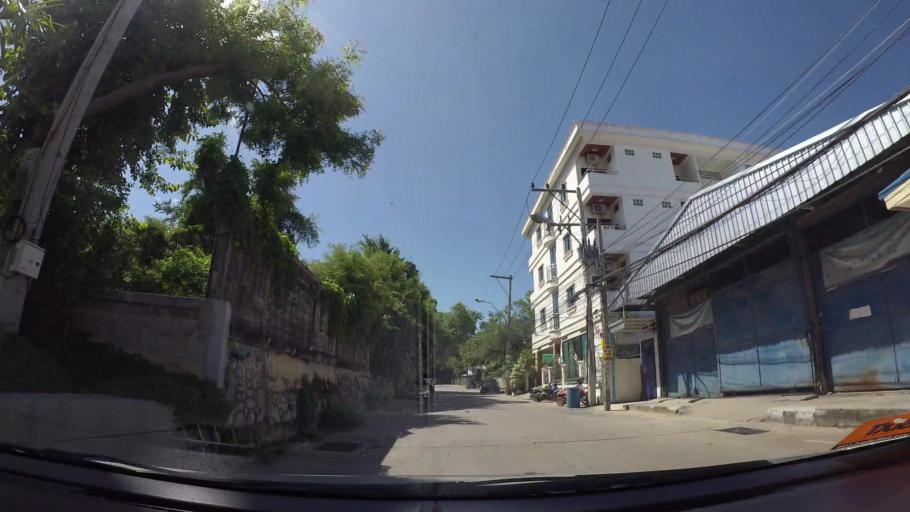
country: TH
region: Chon Buri
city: Phatthaya
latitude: 12.9325
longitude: 100.8954
